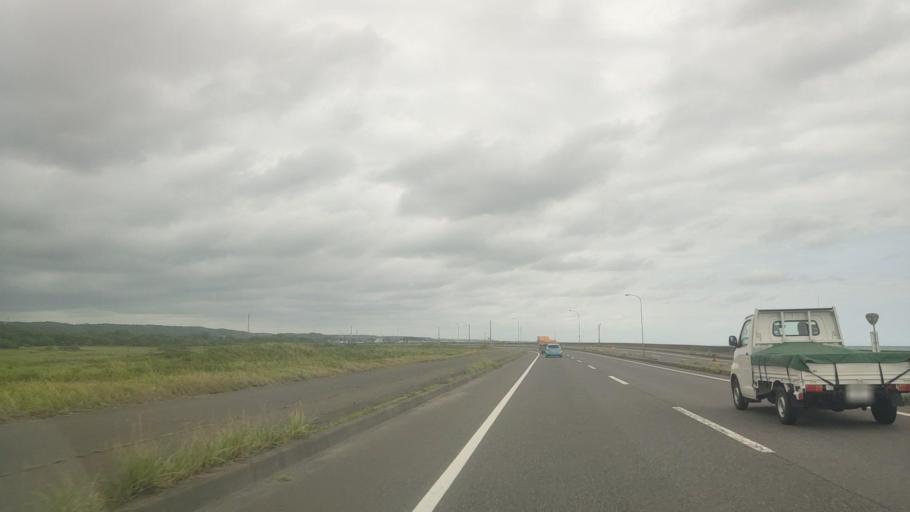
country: JP
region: Hokkaido
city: Shiraoi
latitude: 42.5566
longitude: 141.3775
